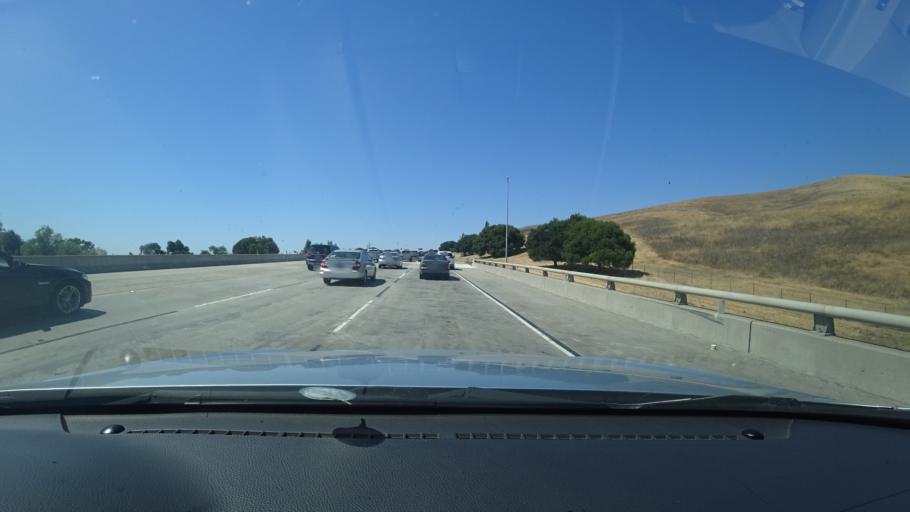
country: US
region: California
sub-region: Santa Clara County
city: Milpitas
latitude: 37.4745
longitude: -121.9107
